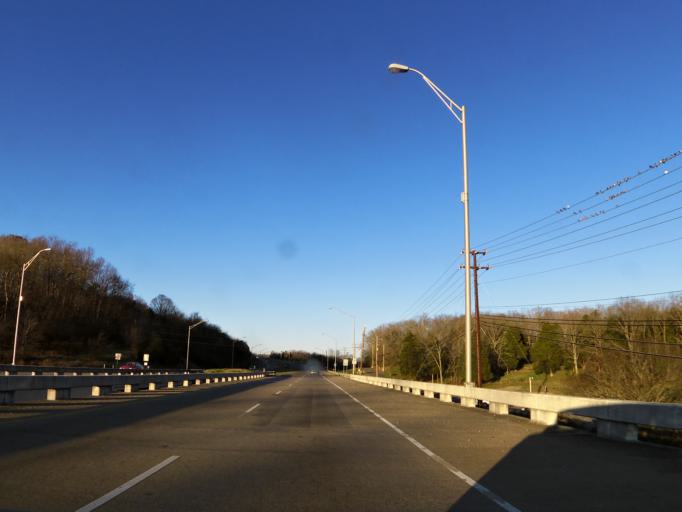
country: US
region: Tennessee
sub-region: Anderson County
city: Clinton
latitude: 36.1233
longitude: -84.1142
